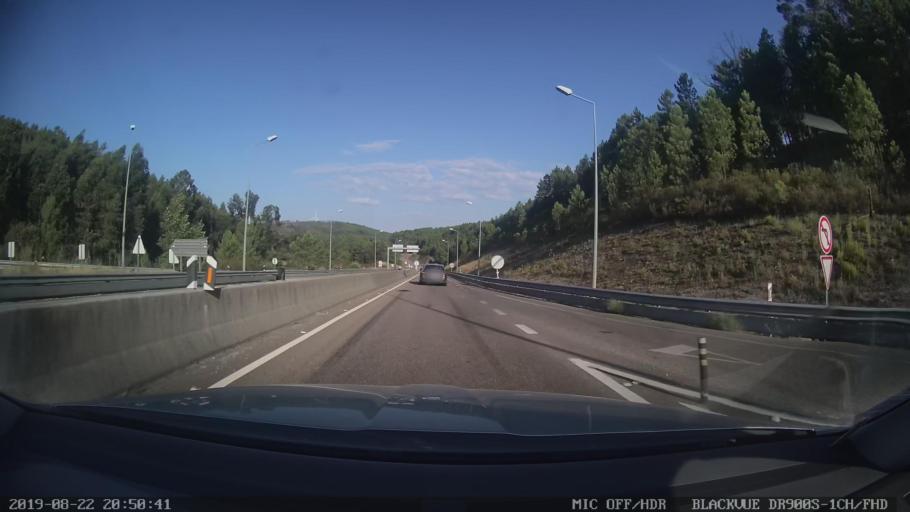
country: PT
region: Castelo Branco
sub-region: Proenca-A-Nova
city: Proenca-a-Nova
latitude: 39.7565
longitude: -7.9434
